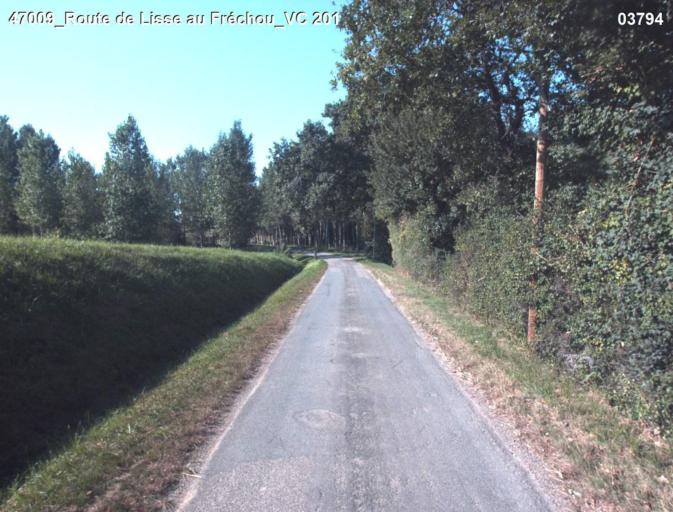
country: FR
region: Aquitaine
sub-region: Departement du Lot-et-Garonne
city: Mezin
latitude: 44.1027
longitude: 0.2754
